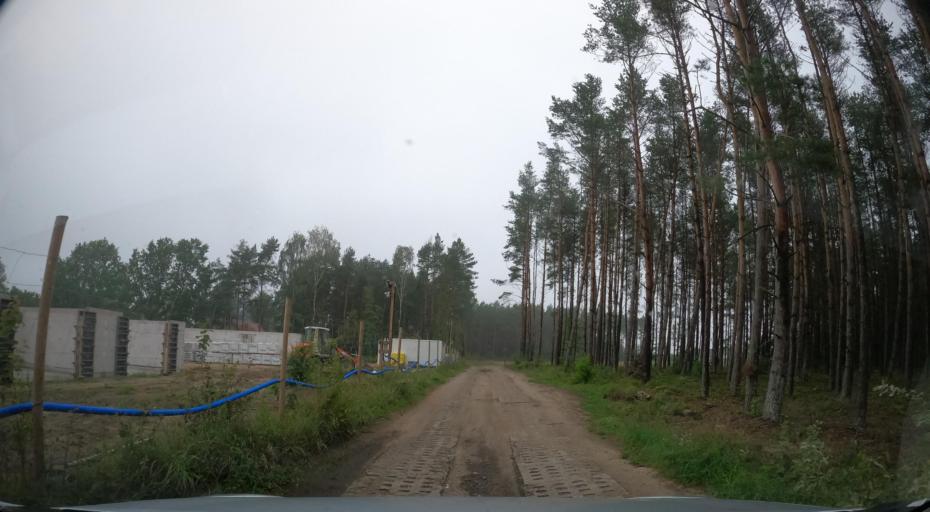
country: PL
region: Pomeranian Voivodeship
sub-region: Powiat kartuski
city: Chwaszczyno
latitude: 54.4356
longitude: 18.4165
